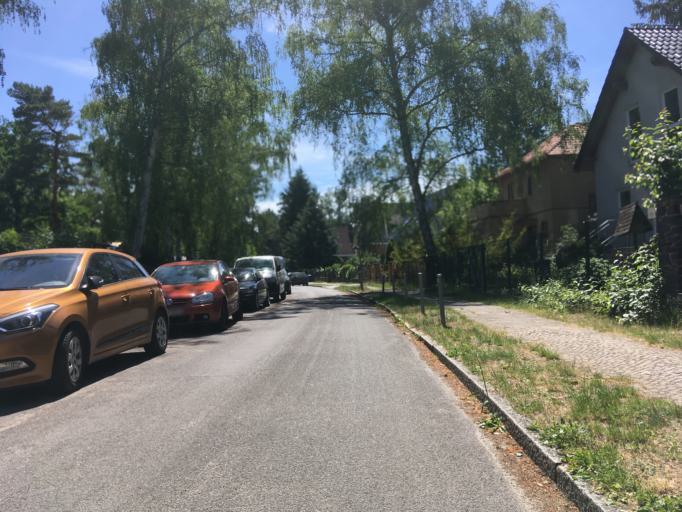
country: DE
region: Berlin
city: Schmockwitz
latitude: 52.3889
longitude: 13.6404
